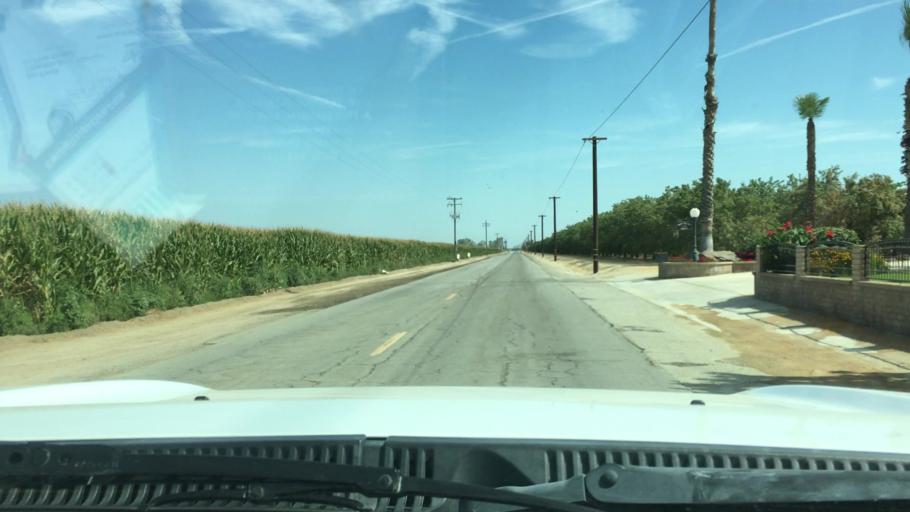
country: US
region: California
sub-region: Kern County
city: Buttonwillow
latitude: 35.4205
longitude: -119.3763
